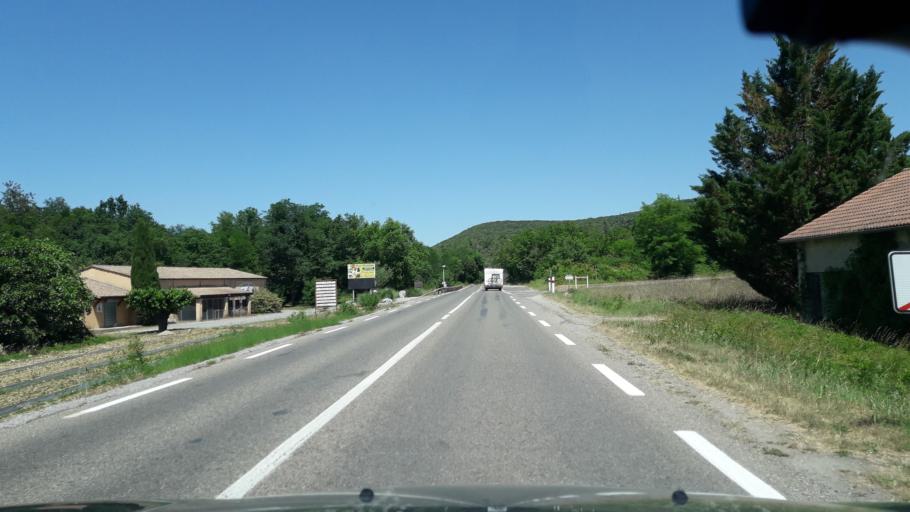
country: FR
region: Rhone-Alpes
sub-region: Departement de l'Ardeche
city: Ruoms
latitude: 44.4099
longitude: 4.2965
